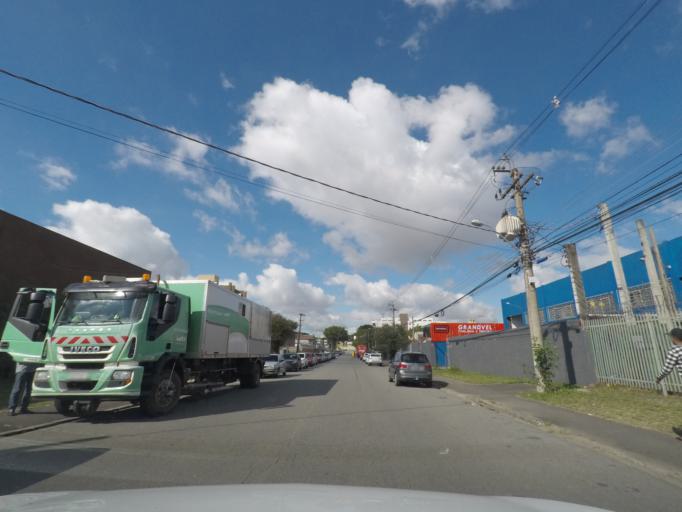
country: BR
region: Parana
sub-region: Curitiba
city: Curitiba
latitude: -25.4514
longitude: -49.2564
